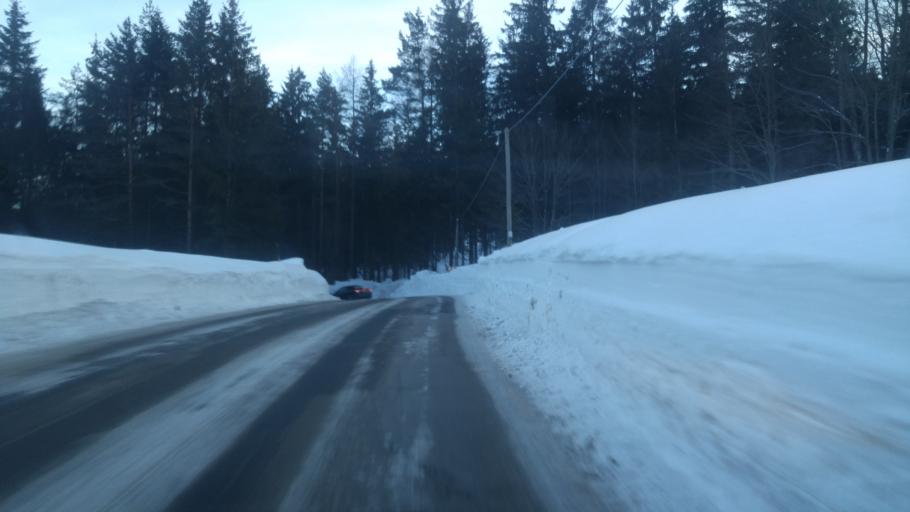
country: AT
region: Lower Austria
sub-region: Politischer Bezirk Lilienfeld
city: Hohenberg
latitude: 47.8909
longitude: 15.6761
